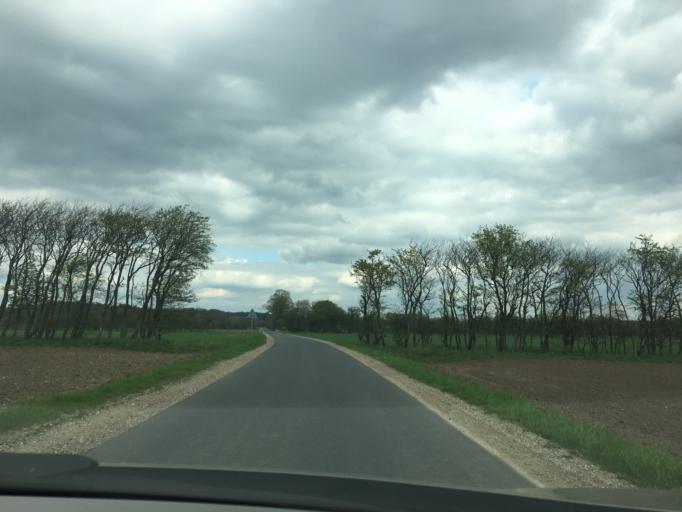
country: DK
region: Central Jutland
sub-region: Horsens Kommune
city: Braedstrup
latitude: 55.9462
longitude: 9.6530
